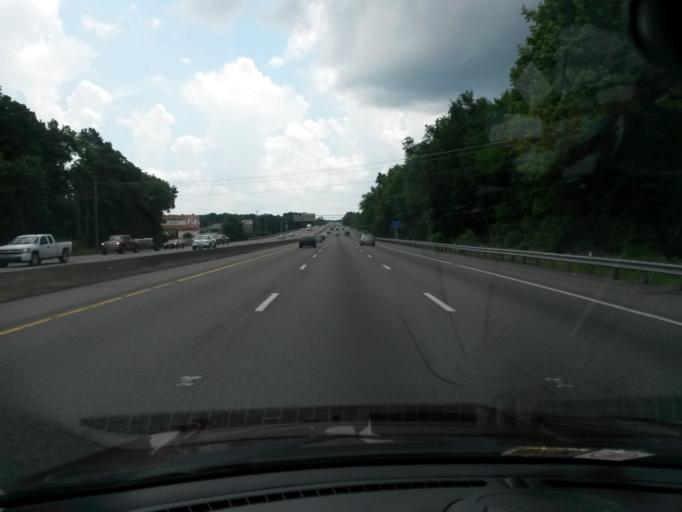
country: US
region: Virginia
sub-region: Chesterfield County
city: Bellwood
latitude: 37.4169
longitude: -77.4275
